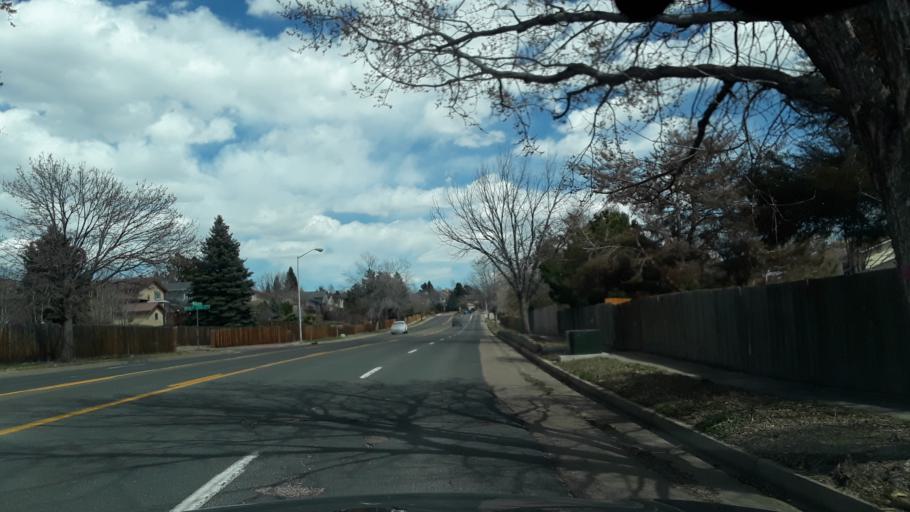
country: US
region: Colorado
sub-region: El Paso County
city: Black Forest
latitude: 38.9431
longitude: -104.7591
